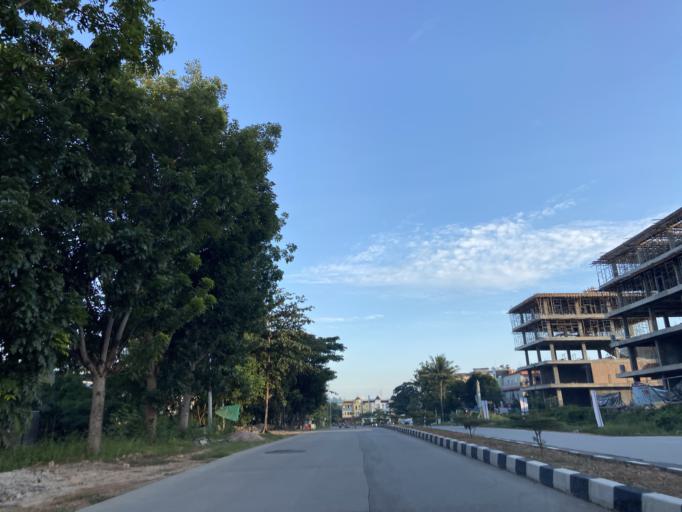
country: SG
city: Singapore
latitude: 1.1276
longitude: 104.0397
